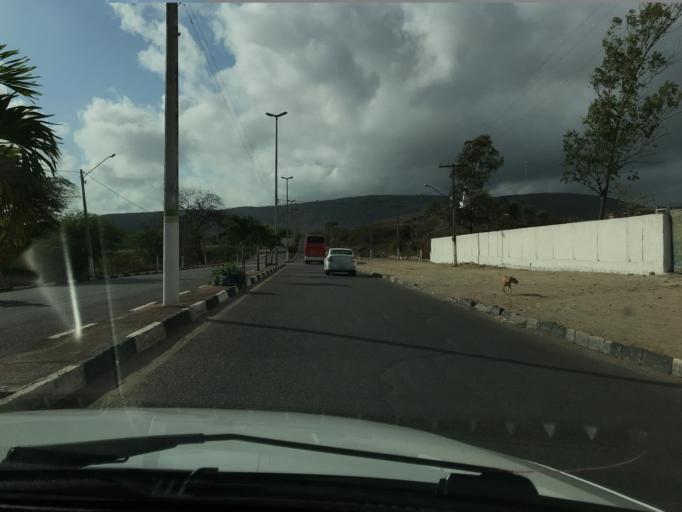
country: BR
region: Pernambuco
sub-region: Bezerros
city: Bezerros
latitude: -8.2336
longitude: -35.7441
